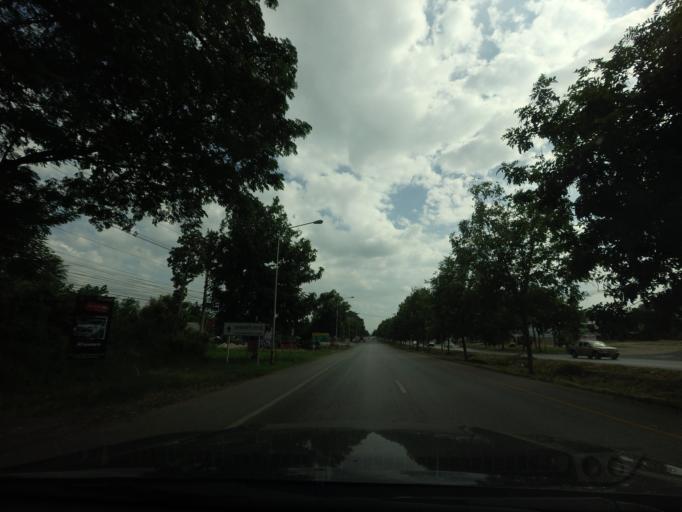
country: TH
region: Lop Buri
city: Chai Badan
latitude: 15.2235
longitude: 101.1274
